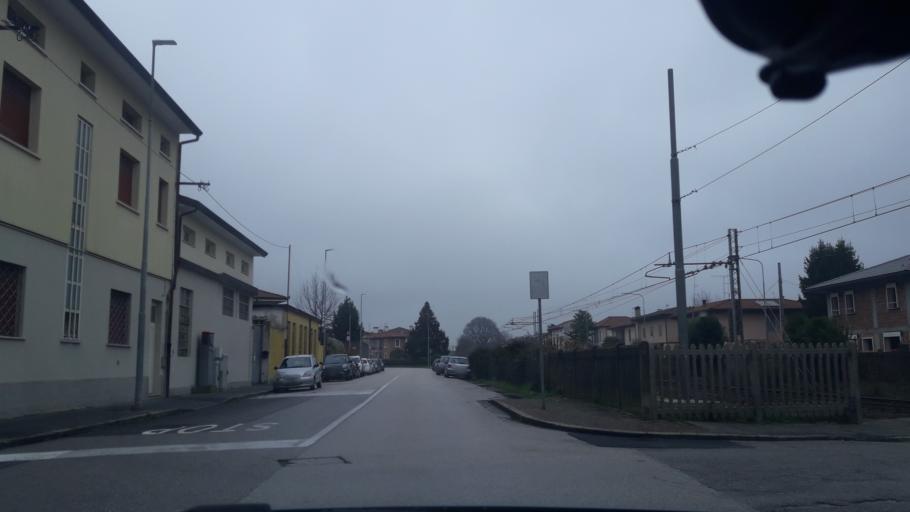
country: IT
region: Friuli Venezia Giulia
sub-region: Provincia di Udine
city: Udine
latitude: 46.0663
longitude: 13.2497
